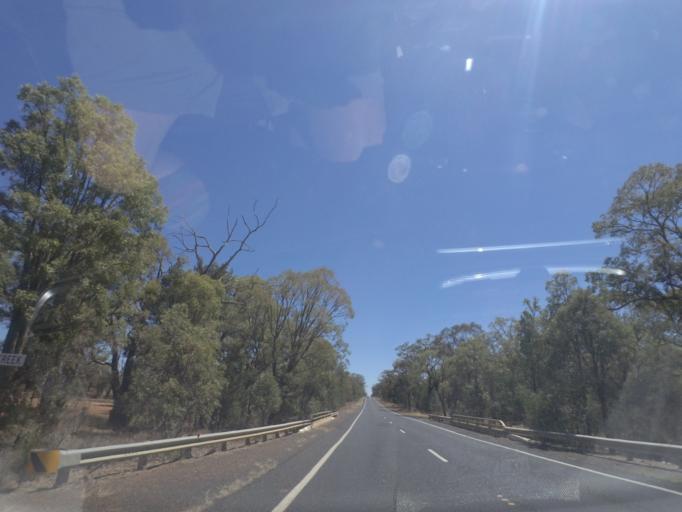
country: AU
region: New South Wales
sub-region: Gilgandra
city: Gilgandra
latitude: -31.4776
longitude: 148.8928
